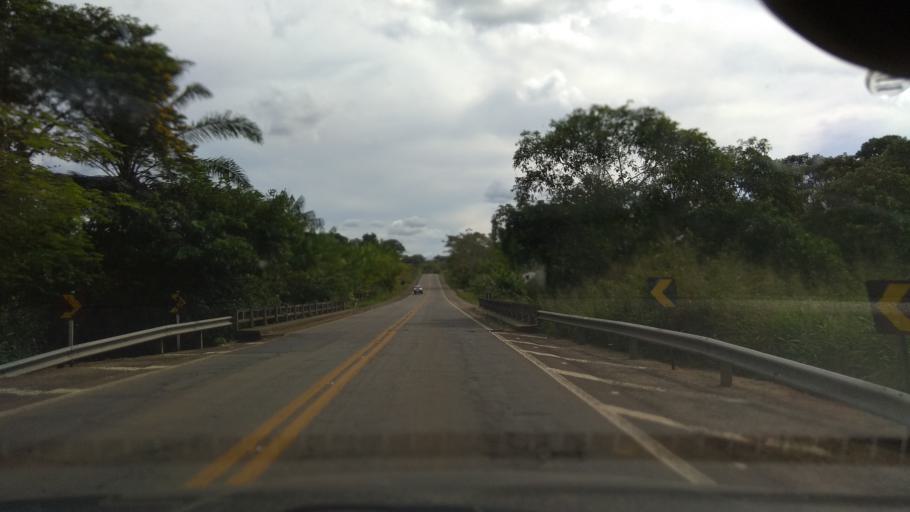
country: BR
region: Bahia
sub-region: Ubata
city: Ubata
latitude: -14.2292
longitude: -39.4406
